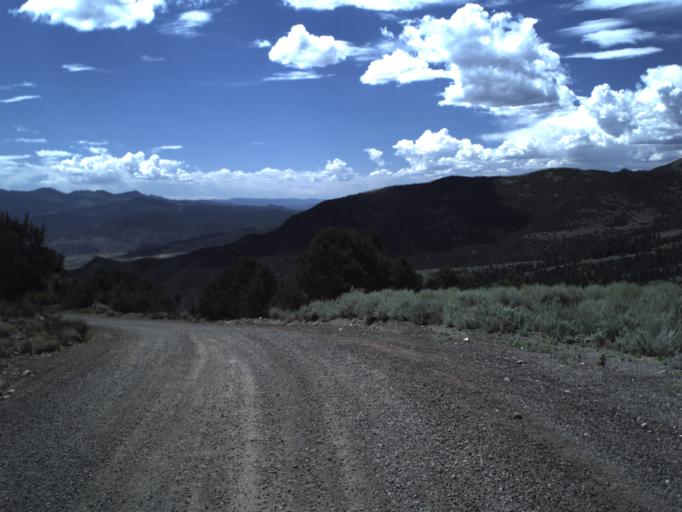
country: US
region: Utah
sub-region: Piute County
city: Junction
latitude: 38.2500
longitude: -112.3130
